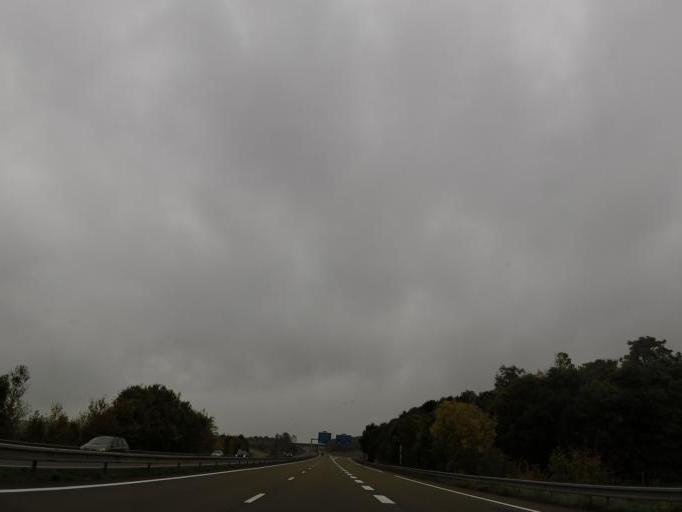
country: FR
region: Champagne-Ardenne
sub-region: Departement de la Marne
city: Fagnieres
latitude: 49.0595
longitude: 4.2818
